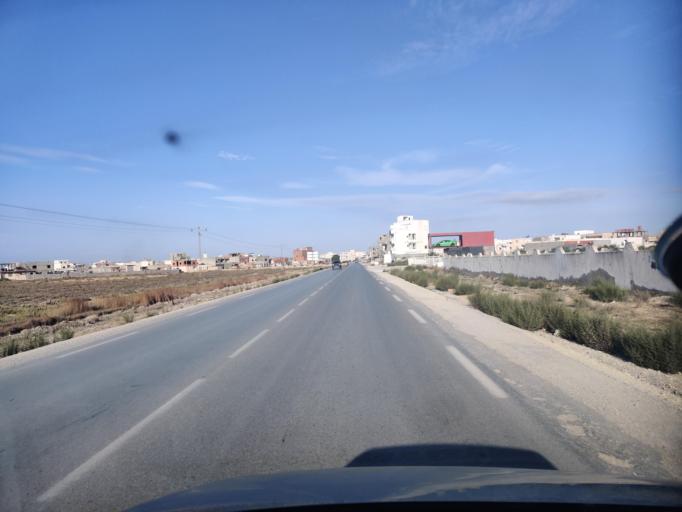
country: TN
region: Ariana
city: Ariana
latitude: 36.9551
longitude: 10.2276
